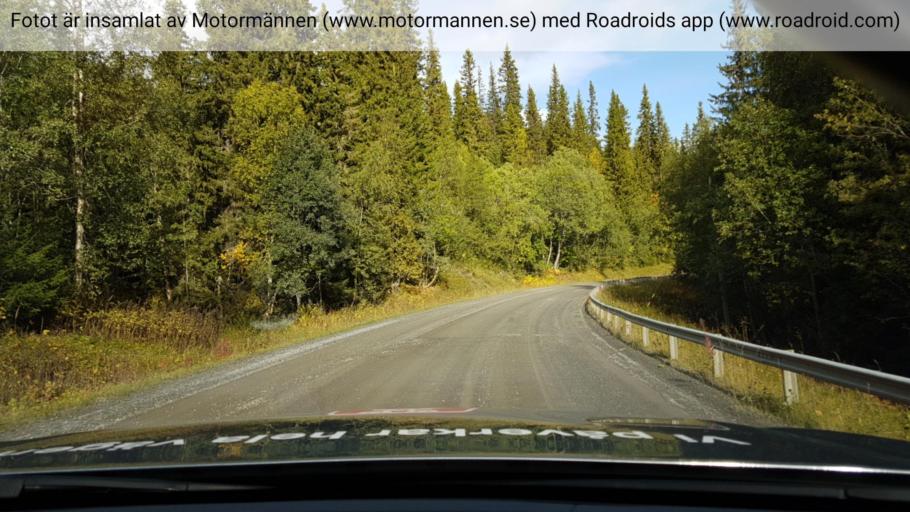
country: SE
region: Jaemtland
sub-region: Are Kommun
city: Are
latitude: 63.6838
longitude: 12.9019
